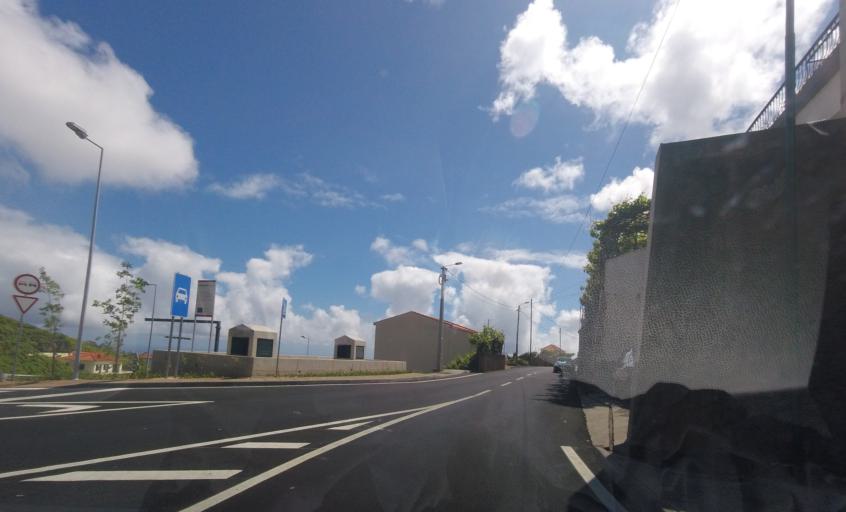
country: PT
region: Madeira
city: Camara de Lobos
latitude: 32.6741
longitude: -16.9738
